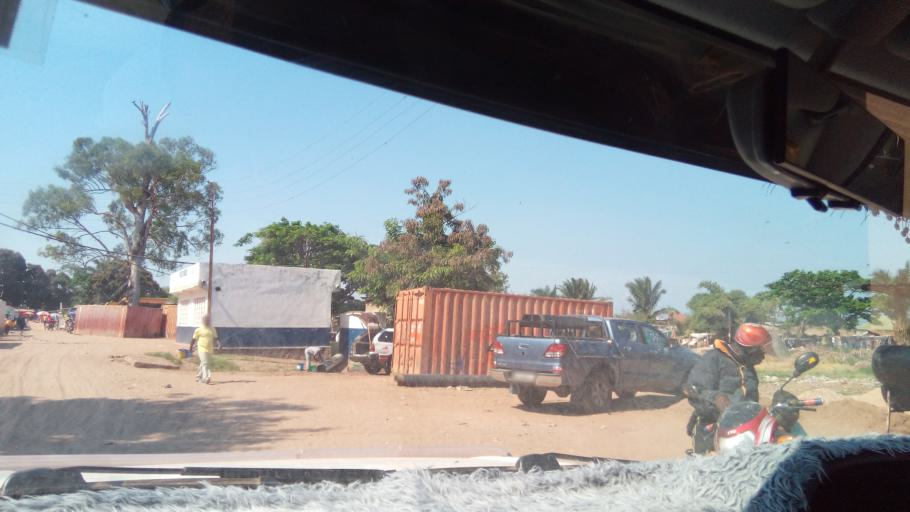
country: CD
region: Katanga
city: Kalemie
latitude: -5.9541
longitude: 29.1956
